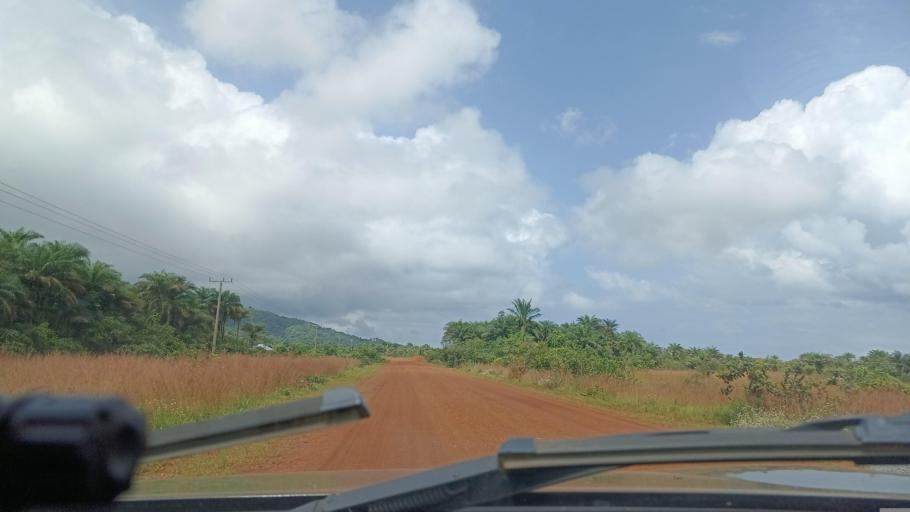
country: LR
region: Grand Cape Mount
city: Robertsport
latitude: 6.7482
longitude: -11.3437
